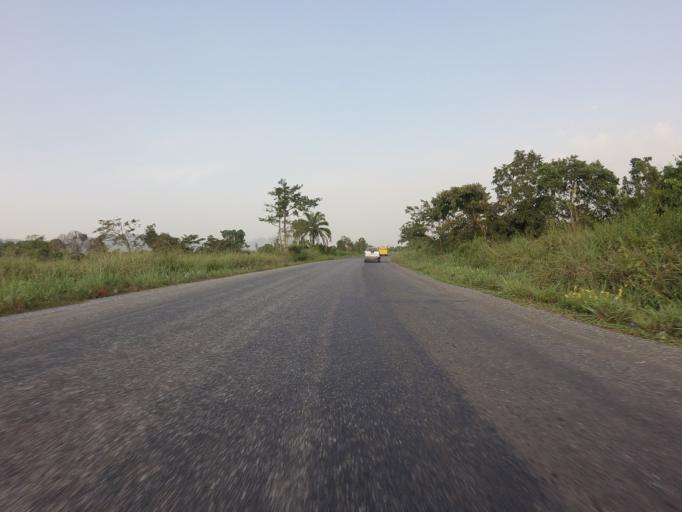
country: GH
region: Volta
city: Ho
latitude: 6.4658
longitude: 0.2223
